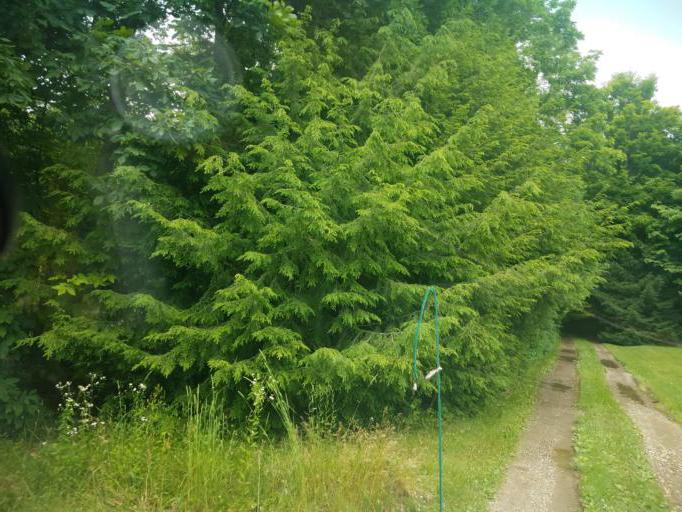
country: US
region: Ohio
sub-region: Sandusky County
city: Bellville
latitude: 40.5656
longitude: -82.4798
